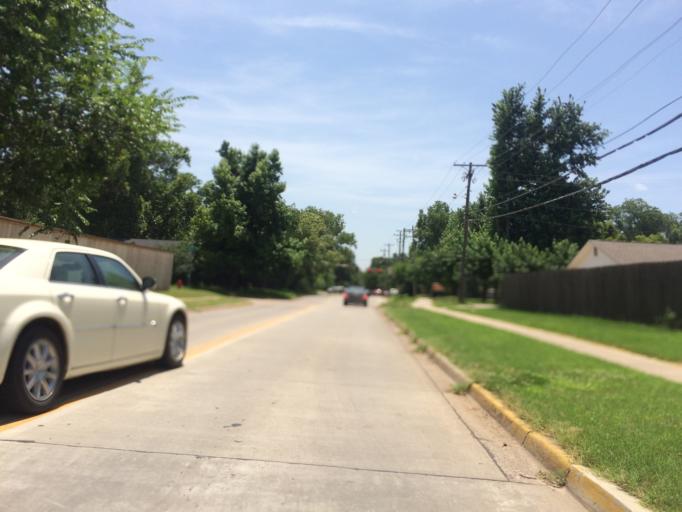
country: US
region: Oklahoma
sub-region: Cleveland County
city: Norman
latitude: 35.2125
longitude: -97.4590
